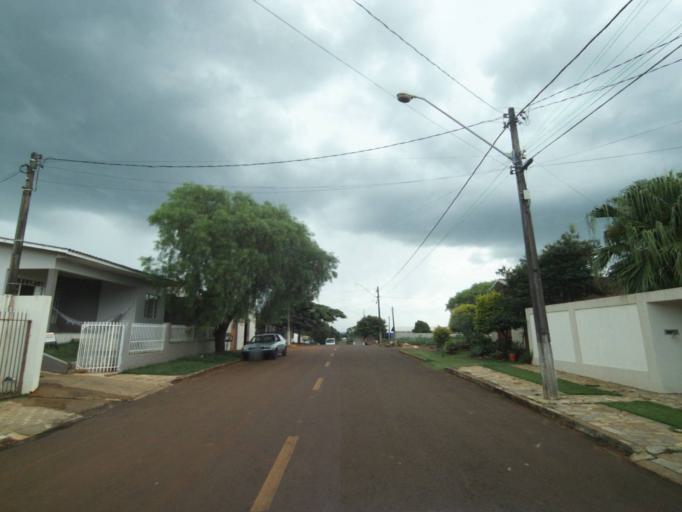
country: BR
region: Parana
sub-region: Guaraniacu
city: Guaraniacu
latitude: -25.0959
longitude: -52.8729
